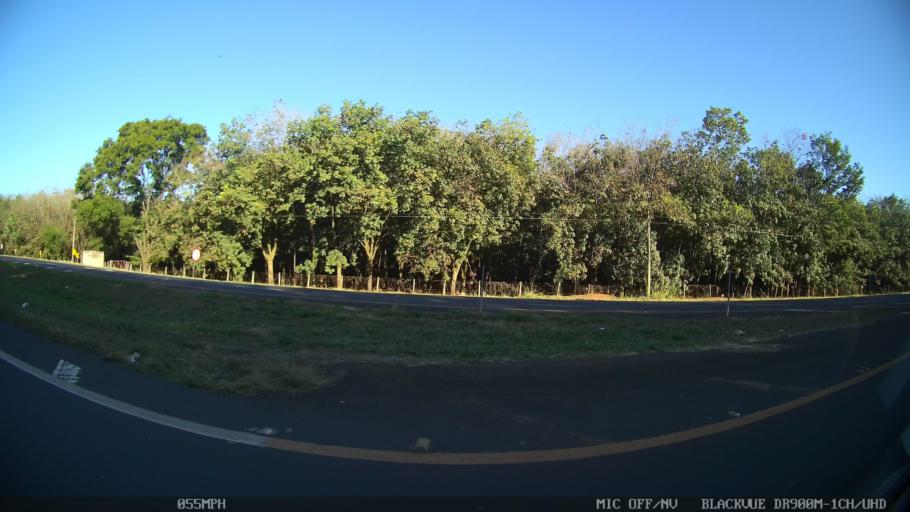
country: BR
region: Sao Paulo
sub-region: Guapiacu
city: Guapiacu
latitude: -20.7619
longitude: -49.1806
